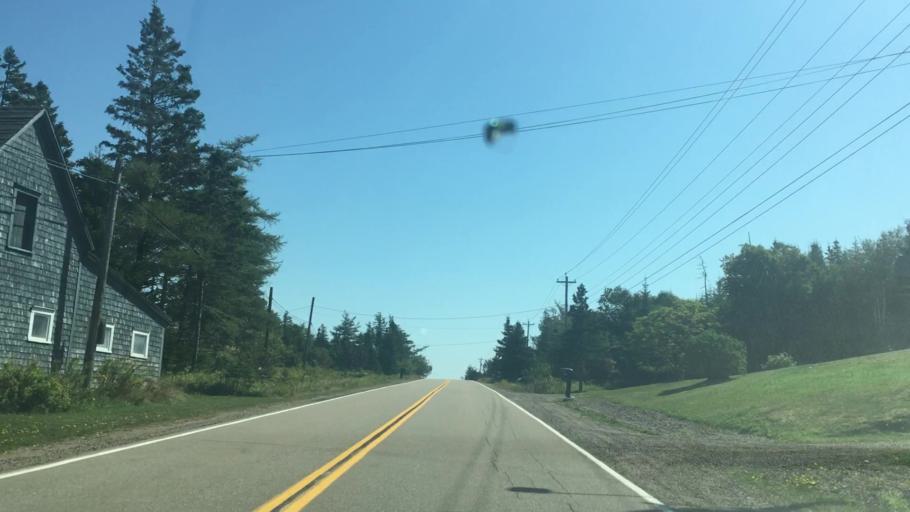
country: CA
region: Nova Scotia
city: Antigonish
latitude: 45.0245
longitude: -62.0242
